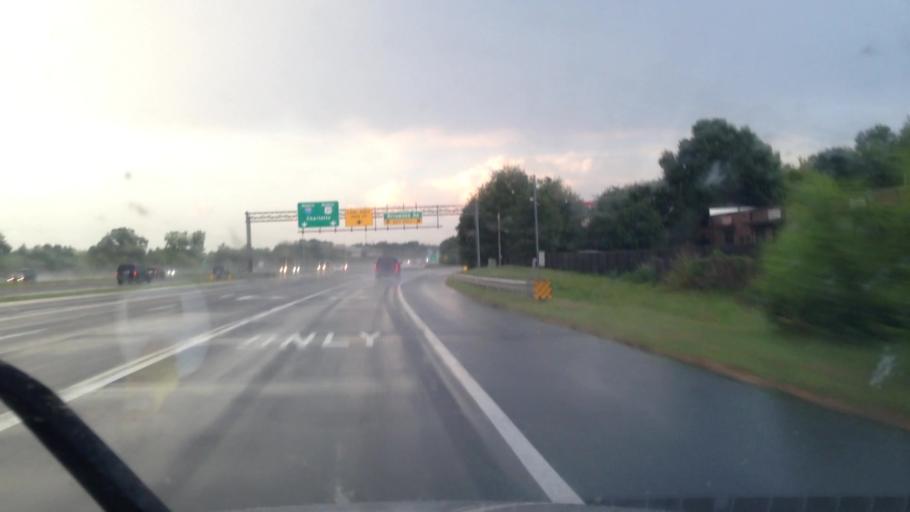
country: US
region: North Carolina
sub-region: Mecklenburg County
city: Pineville
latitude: 35.1335
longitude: -80.9113
